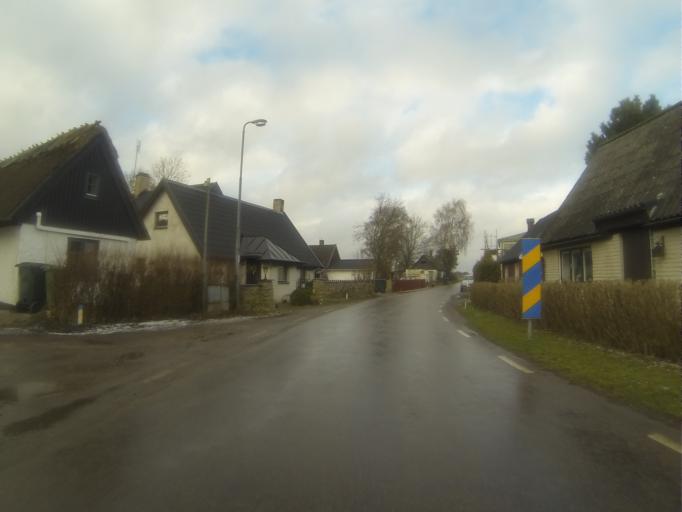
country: SE
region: Skane
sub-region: Svedala Kommun
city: Klagerup
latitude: 55.5722
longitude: 13.3014
